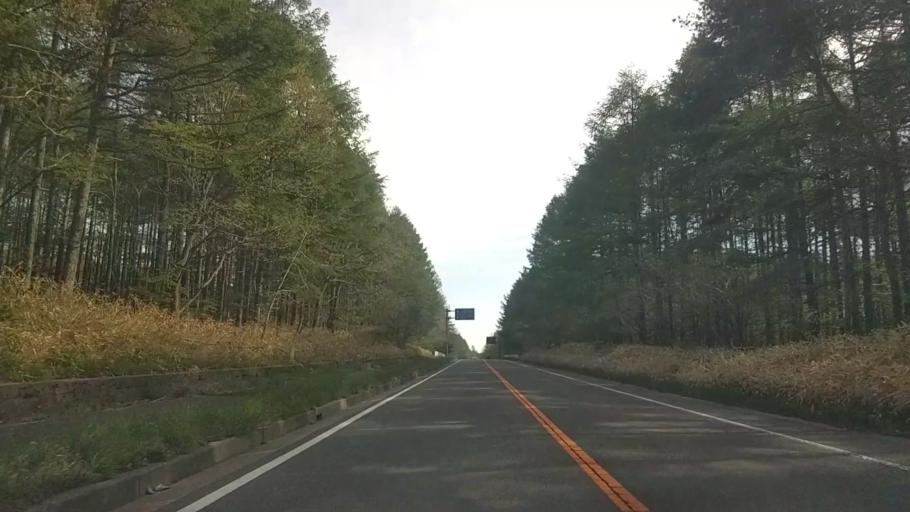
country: JP
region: Yamanashi
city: Nirasaki
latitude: 35.9369
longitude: 138.4481
